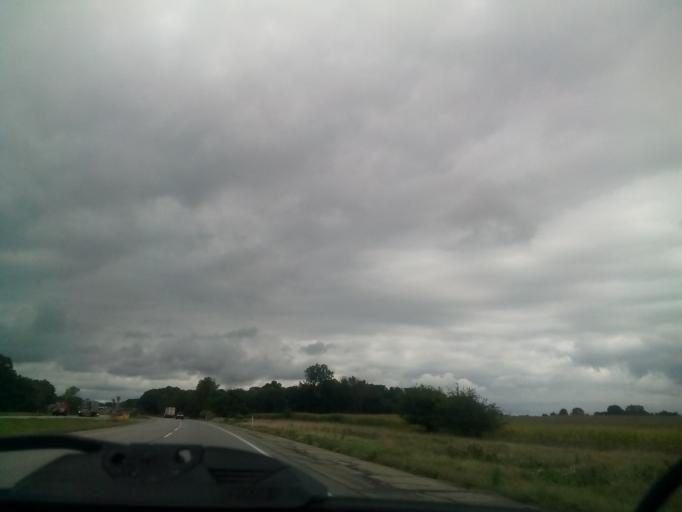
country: US
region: Michigan
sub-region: Branch County
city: Bronson
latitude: 41.7546
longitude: -85.2356
